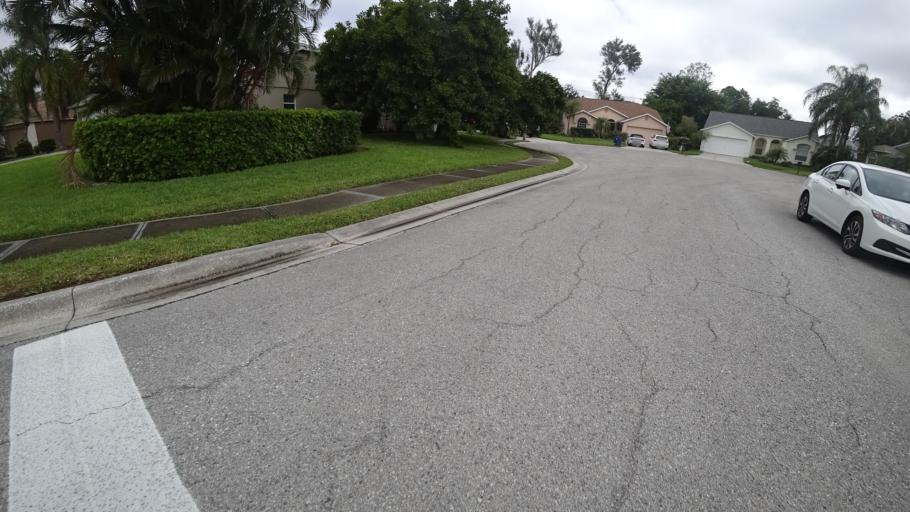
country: US
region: Florida
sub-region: Manatee County
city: South Bradenton
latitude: 27.4509
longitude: -82.6007
